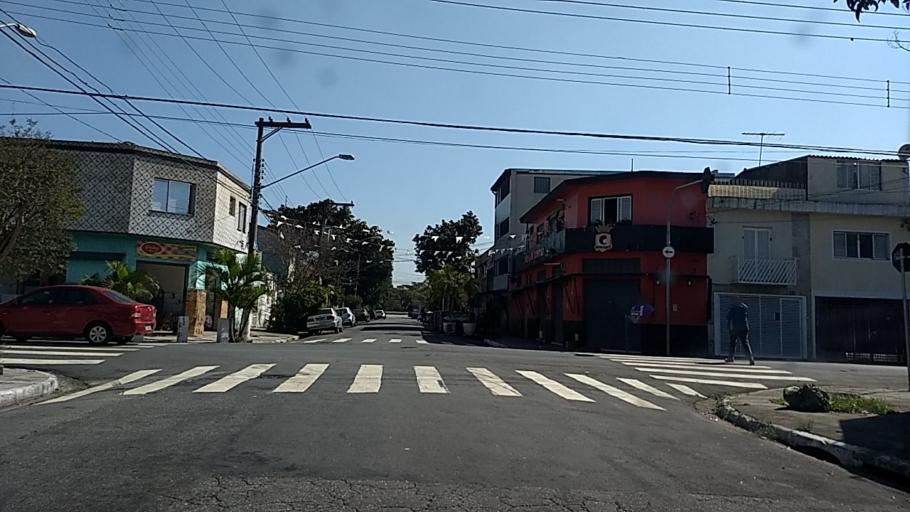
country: BR
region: Sao Paulo
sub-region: Sao Paulo
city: Sao Paulo
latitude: -23.5146
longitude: -46.5935
